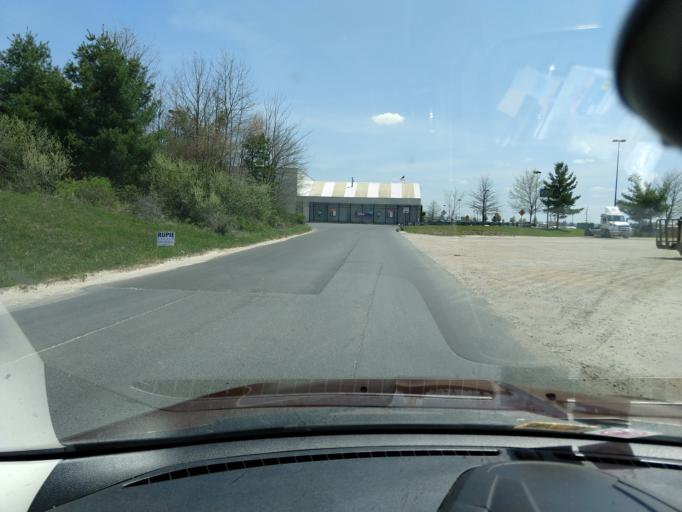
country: US
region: West Virginia
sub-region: Raleigh County
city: Stanaford
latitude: 37.8065
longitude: -81.1786
